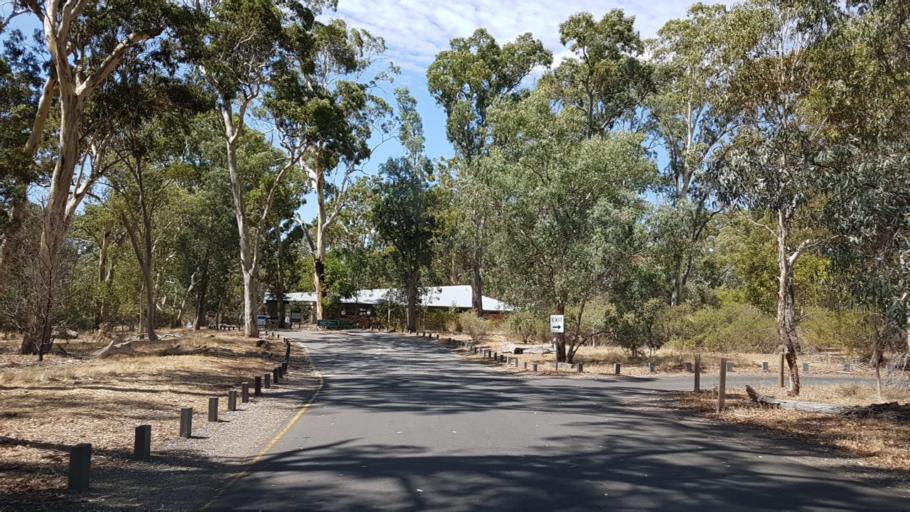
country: AU
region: South Australia
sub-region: Mitcham
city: Belair
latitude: -35.0082
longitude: 138.6356
